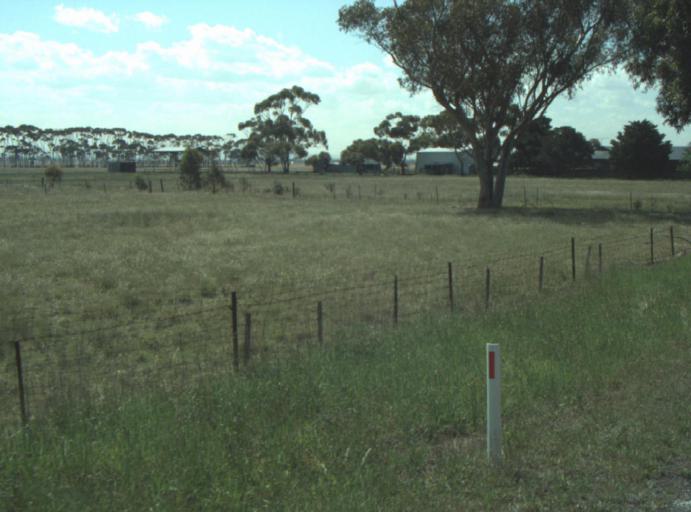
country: AU
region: Victoria
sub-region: Greater Geelong
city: Lara
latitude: -37.9947
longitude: 144.4014
